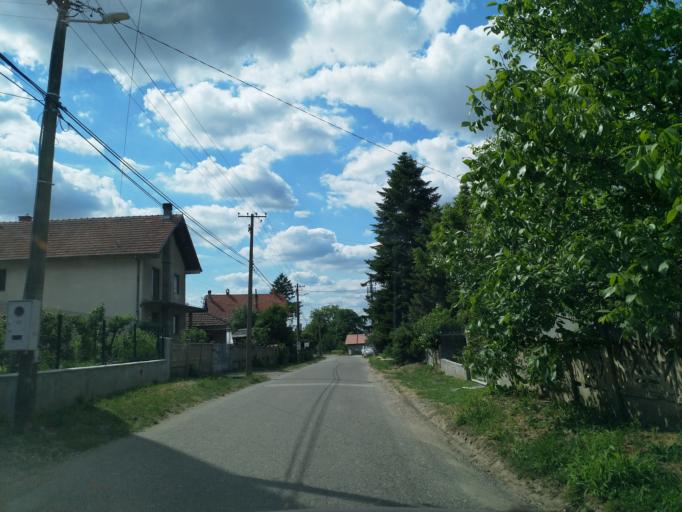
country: RS
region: Central Serbia
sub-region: Pomoravski Okrug
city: Jagodina
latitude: 43.9417
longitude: 21.3006
